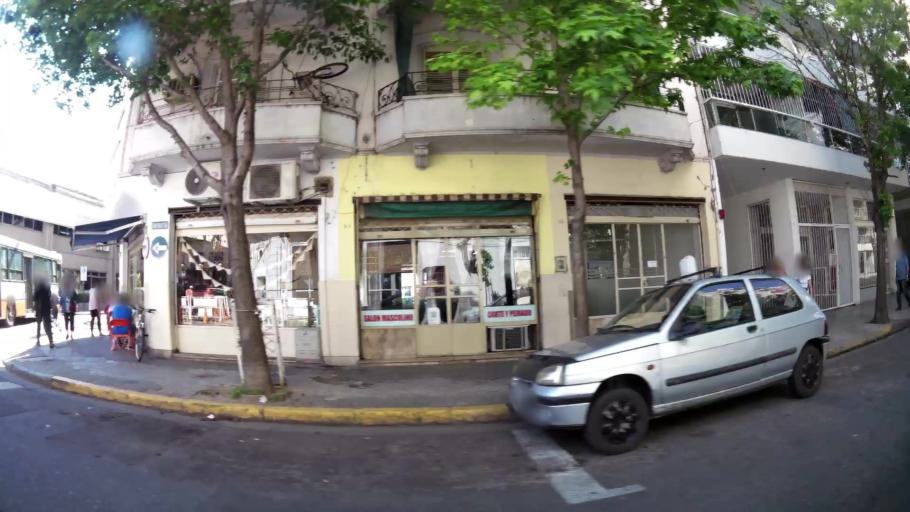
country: AR
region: Santa Fe
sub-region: Departamento de Rosario
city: Rosario
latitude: -32.9566
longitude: -60.6392
